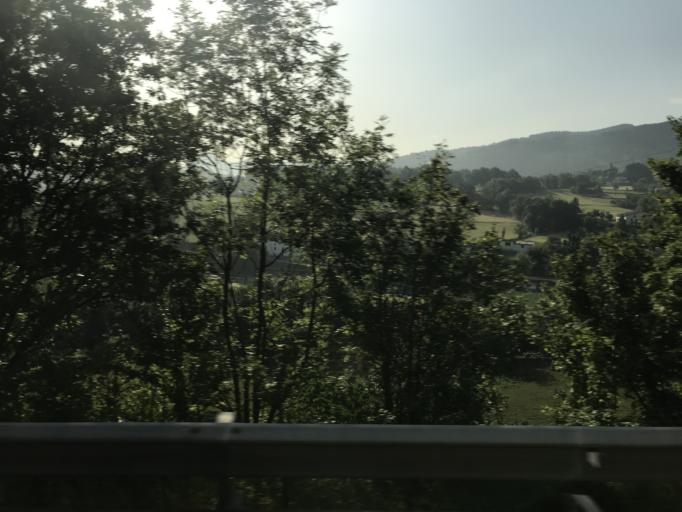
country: ES
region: Basque Country
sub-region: Provincia de Guipuzcoa
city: Idiazabal
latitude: 43.0194
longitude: -2.2349
